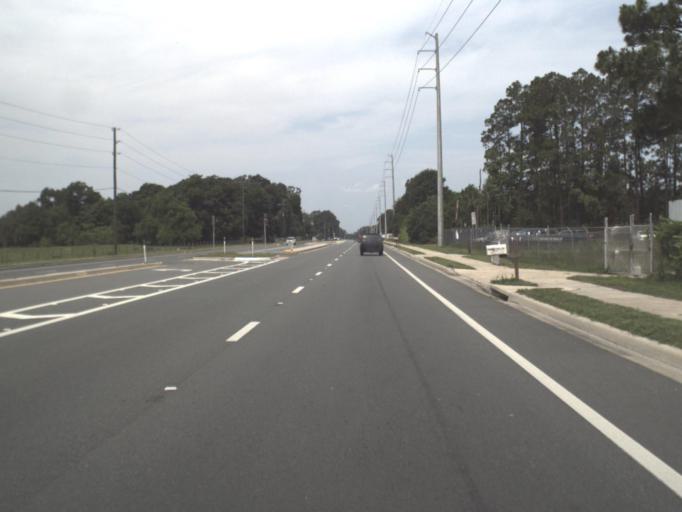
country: US
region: Florida
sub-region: Putnam County
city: Interlachen
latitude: 29.6285
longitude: -81.8359
